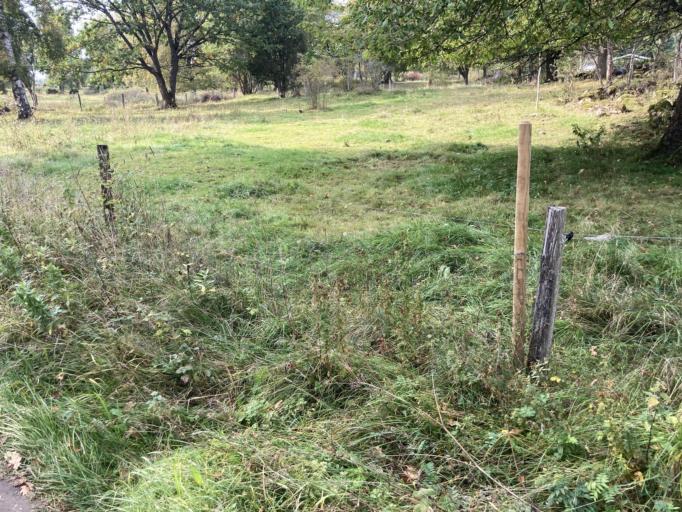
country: SE
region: Vaestra Goetaland
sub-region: Skara Kommun
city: Axvall
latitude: 58.4022
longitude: 13.5925
